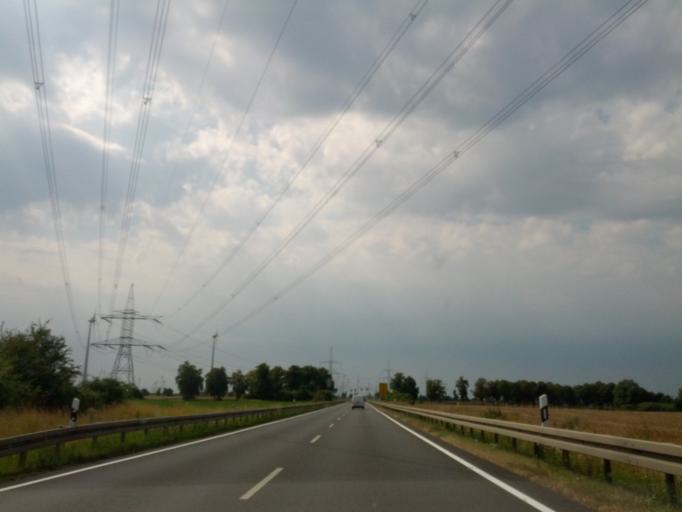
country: DE
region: Brandenburg
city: Nauen
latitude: 52.5928
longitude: 12.8792
